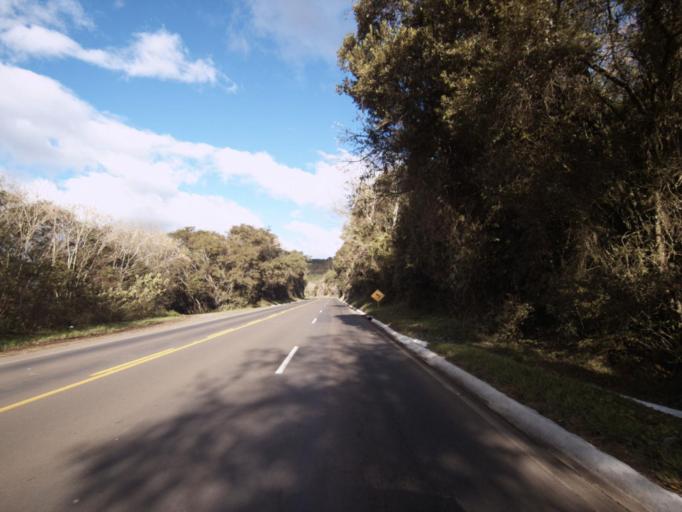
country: BR
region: Santa Catarina
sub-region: Joacaba
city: Joacaba
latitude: -27.2941
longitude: -51.4106
